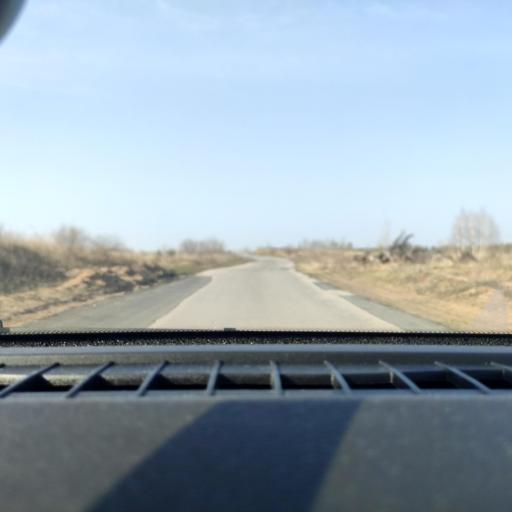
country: RU
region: Samara
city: Tol'yatti
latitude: 53.4908
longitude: 49.3495
